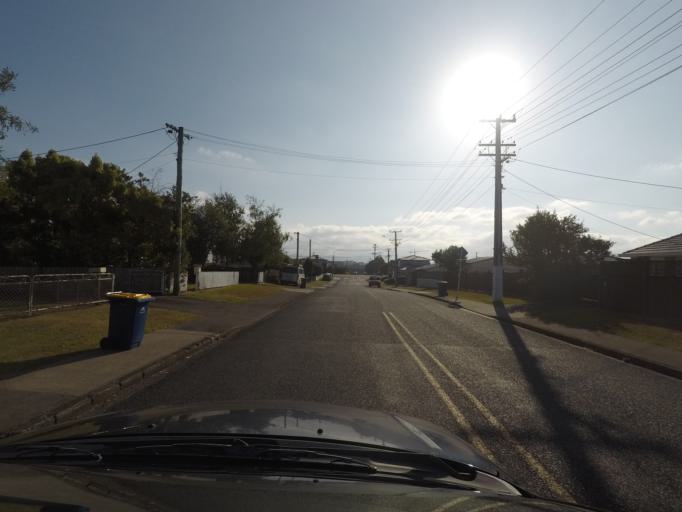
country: NZ
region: Auckland
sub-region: Auckland
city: Rosebank
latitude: -36.8567
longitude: 174.6439
